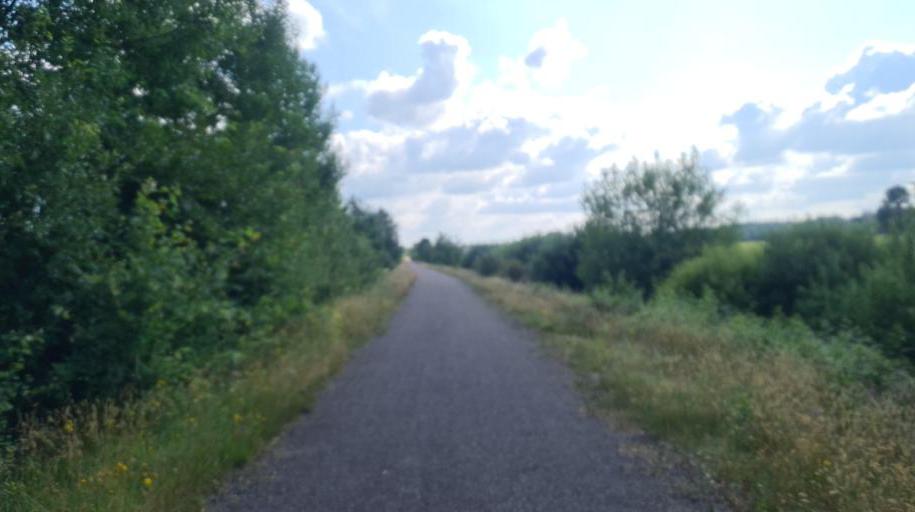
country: SE
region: Kronoberg
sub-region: Ljungby Kommun
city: Ljungby
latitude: 56.7903
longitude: 13.9056
